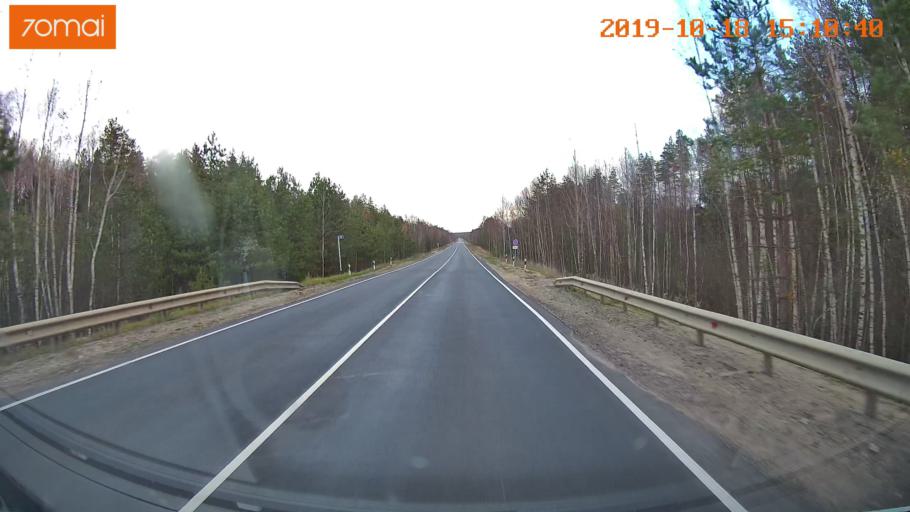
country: RU
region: Vladimir
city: Gus'-Khrustal'nyy
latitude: 55.5687
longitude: 40.6497
